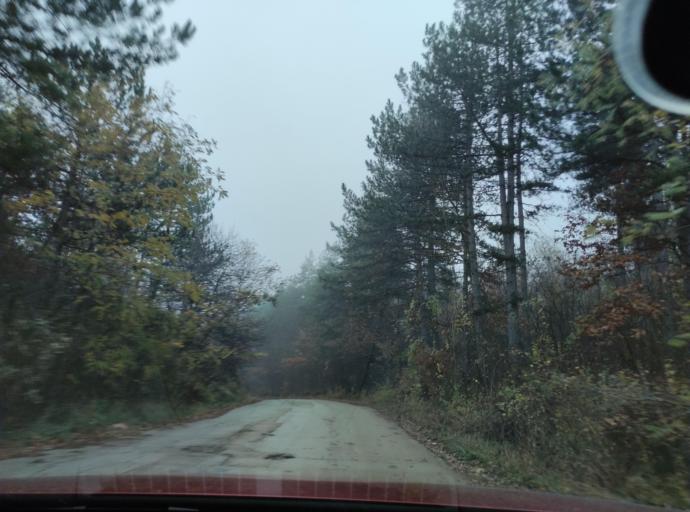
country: BG
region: Lovech
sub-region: Obshtina Yablanitsa
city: Yablanitsa
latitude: 43.1043
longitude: 24.0675
